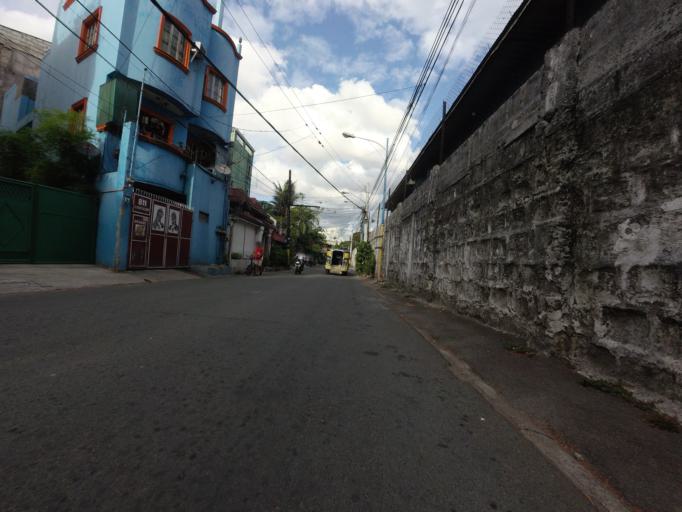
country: PH
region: Metro Manila
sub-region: Mandaluyong
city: Mandaluyong City
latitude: 14.5696
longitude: 121.0378
